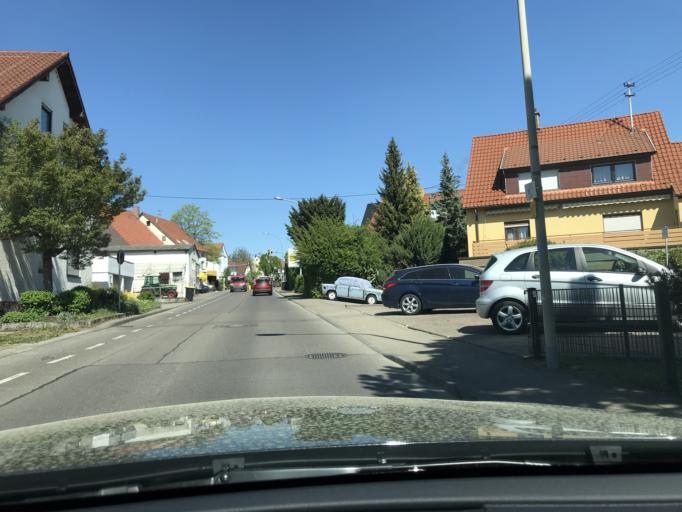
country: DE
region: Baden-Wuerttemberg
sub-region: Regierungsbezirk Stuttgart
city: Korb
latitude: 48.8386
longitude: 9.3551
